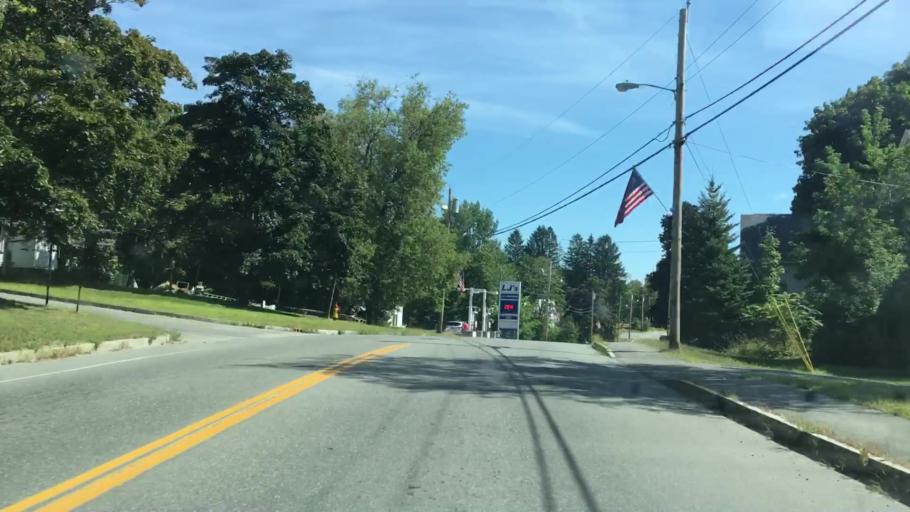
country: US
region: Maine
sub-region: Piscataquis County
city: Milo
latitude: 45.2518
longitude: -68.9851
